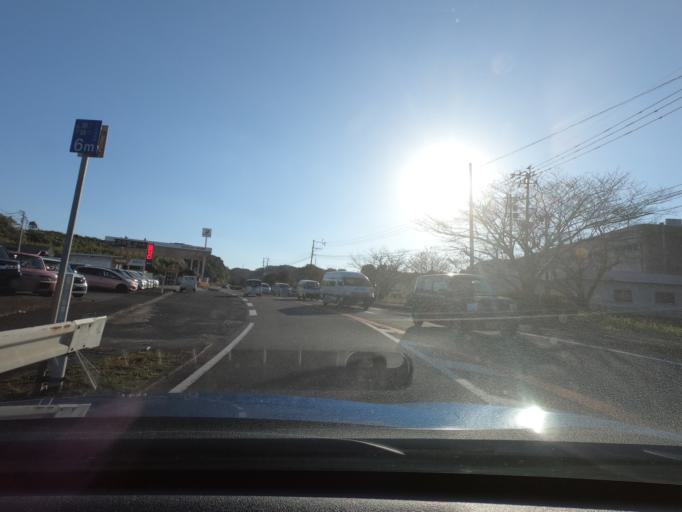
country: JP
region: Kagoshima
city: Akune
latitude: 32.0595
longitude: 130.2226
